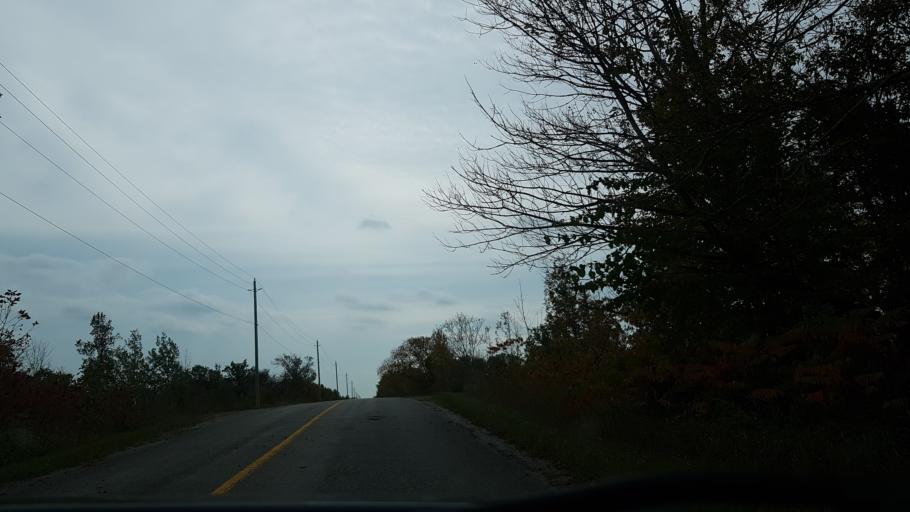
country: CA
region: Ontario
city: Orillia
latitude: 44.6886
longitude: -78.9833
